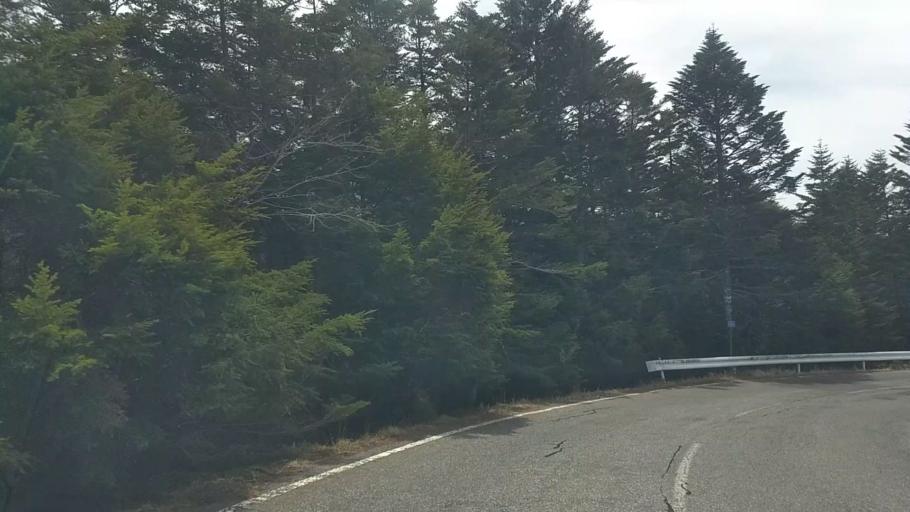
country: JP
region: Nagano
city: Chino
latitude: 36.0571
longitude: 138.3280
